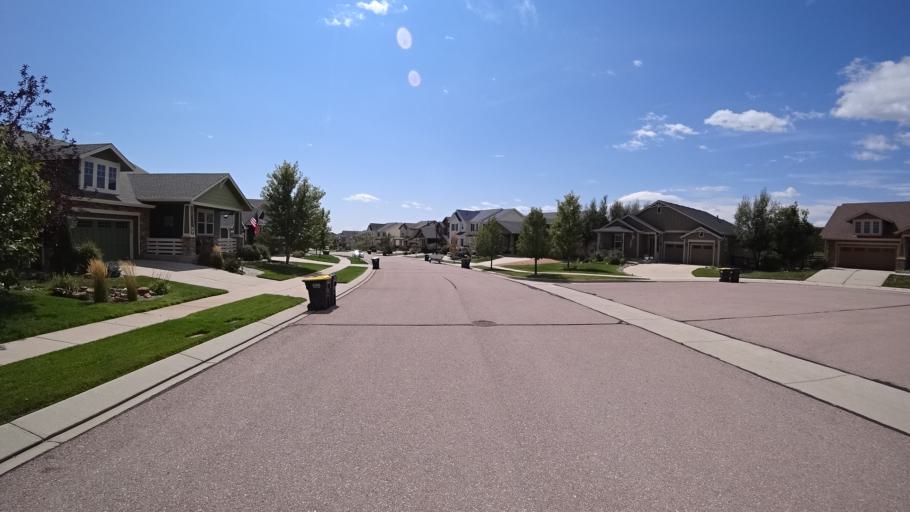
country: US
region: Colorado
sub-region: El Paso County
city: Cimarron Hills
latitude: 38.9292
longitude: -104.6768
